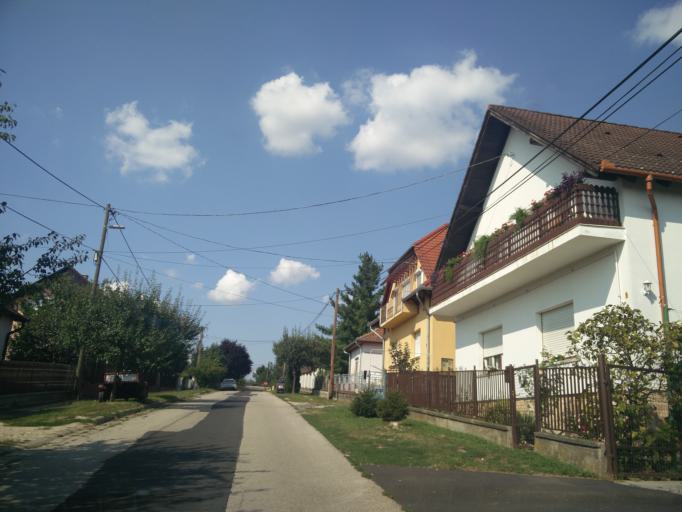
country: HU
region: Zala
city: Zalaegerszeg
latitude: 46.8554
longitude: 16.8281
